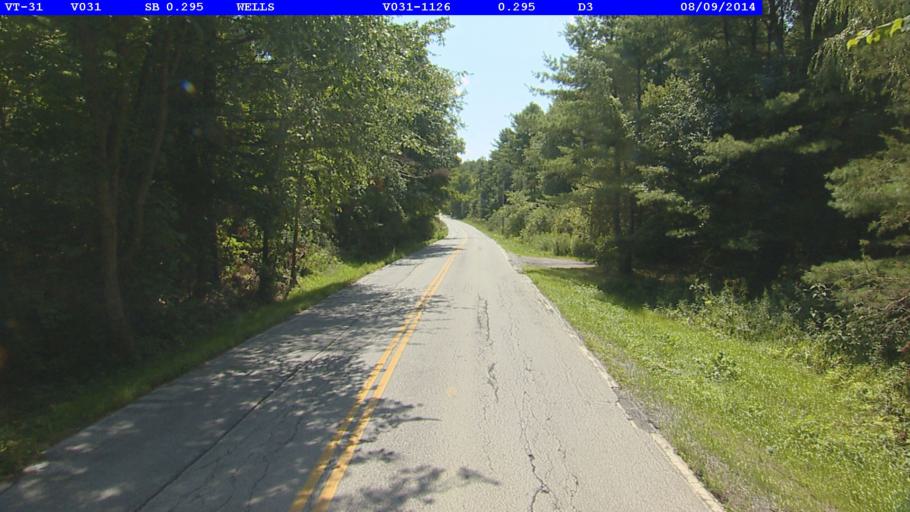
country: US
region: New York
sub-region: Washington County
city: Granville
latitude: 43.4423
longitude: -73.2480
